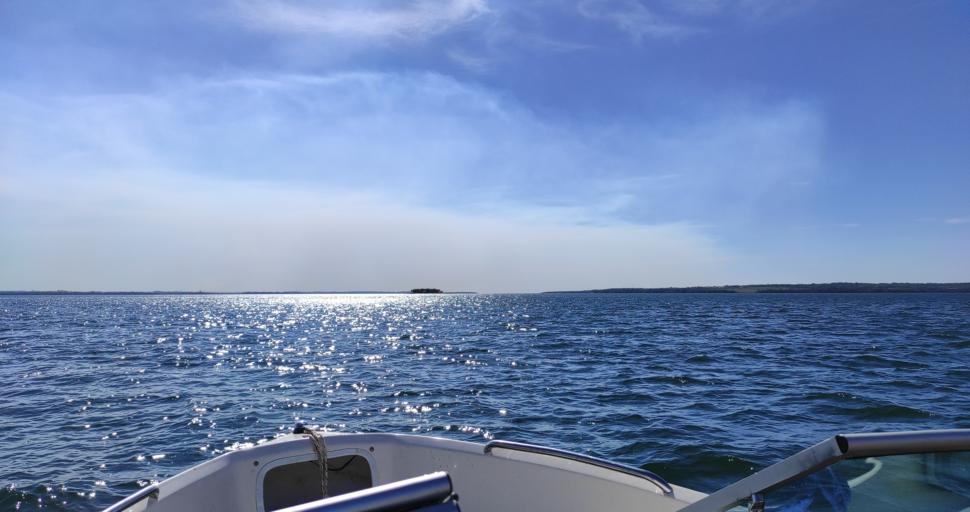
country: AR
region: Misiones
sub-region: Departamento de Capital
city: Posadas
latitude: -27.3431
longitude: -55.9323
